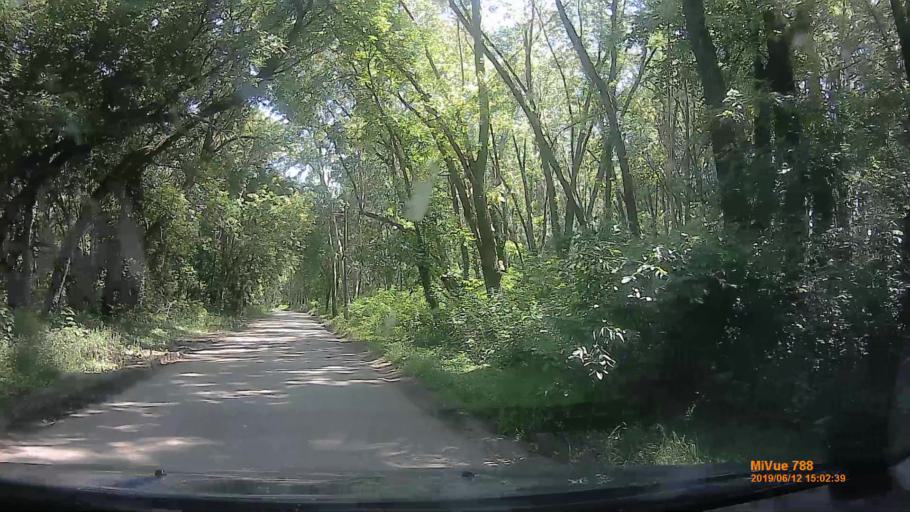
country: HU
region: Csongrad
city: Mako
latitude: 46.2062
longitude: 20.4639
